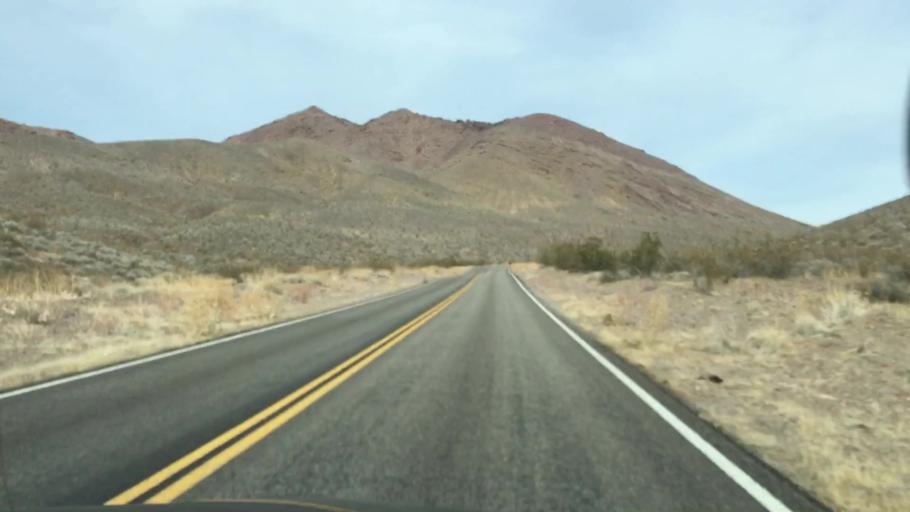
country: US
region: Nevada
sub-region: Nye County
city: Beatty
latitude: 36.7723
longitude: -116.9318
